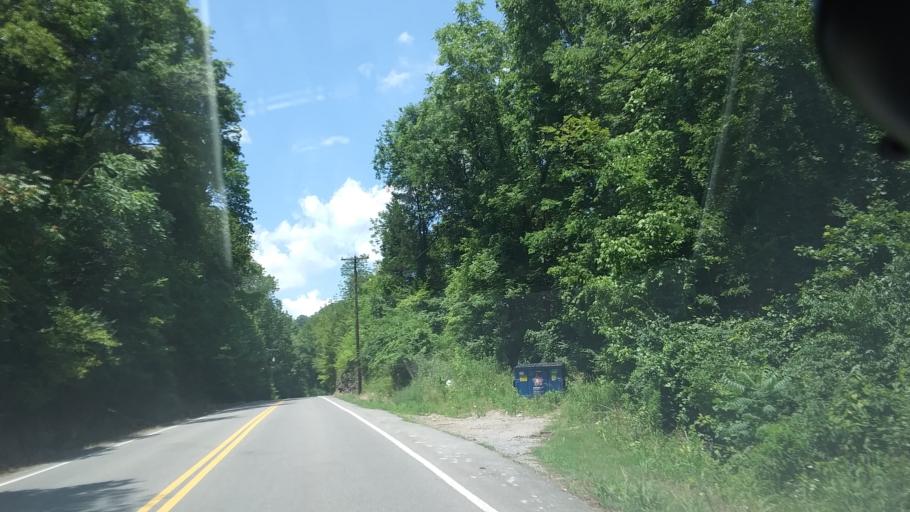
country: US
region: Tennessee
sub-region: Davidson County
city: Belle Meade
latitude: 36.1249
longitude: -86.9266
